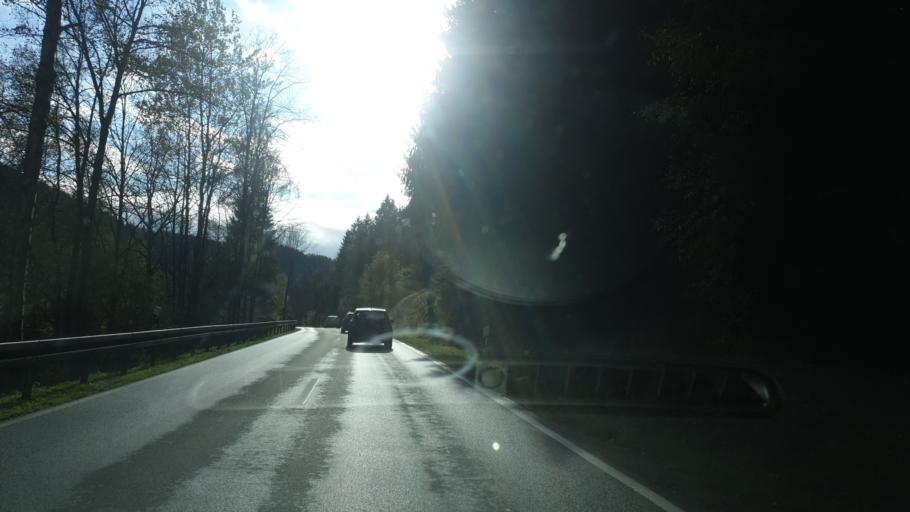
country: DE
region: Saxony
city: Zschorlau
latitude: 50.5348
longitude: 12.6515
